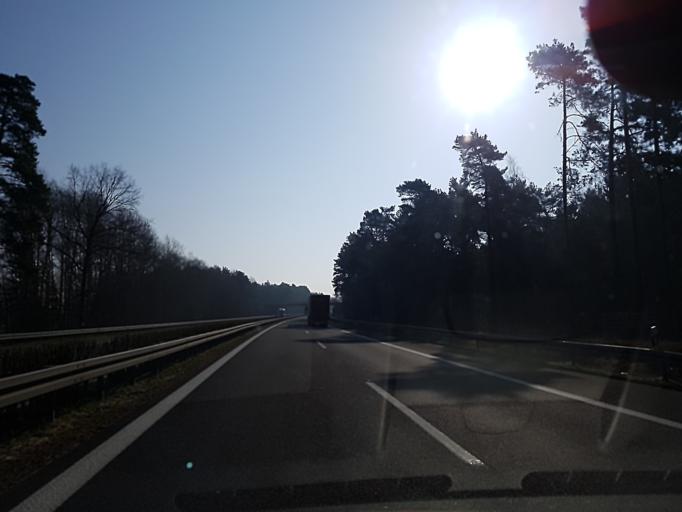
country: DE
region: Brandenburg
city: Forst
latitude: 51.7131
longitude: 14.5980
